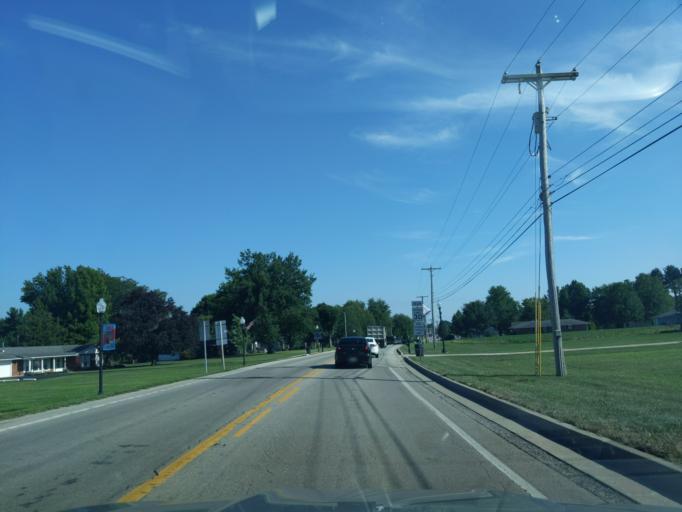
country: US
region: Indiana
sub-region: Ripley County
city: Osgood
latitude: 39.1399
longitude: -85.2947
